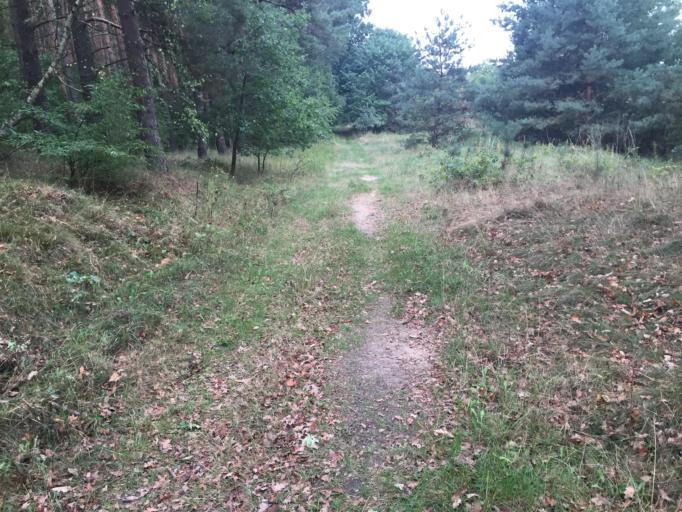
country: DE
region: Brandenburg
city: Grossbeeren
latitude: 52.3280
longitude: 13.2924
